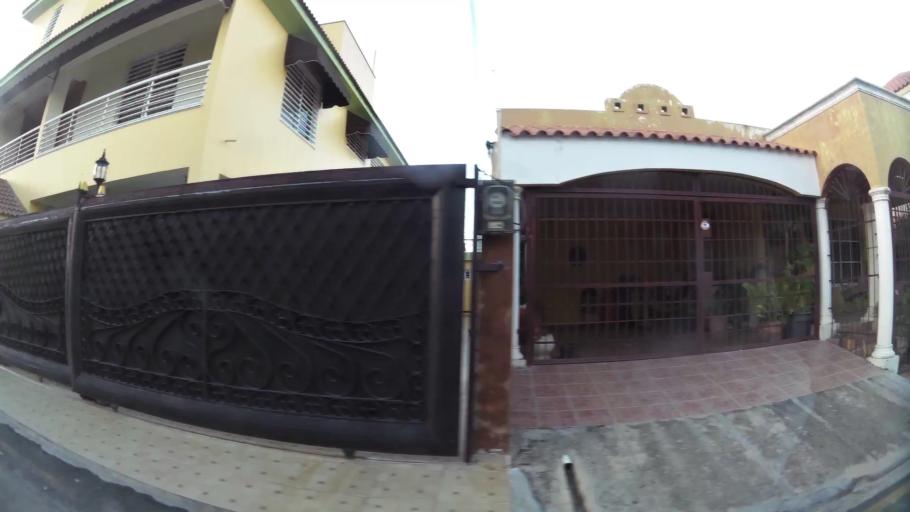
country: DO
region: Santo Domingo
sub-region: Santo Domingo
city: Santo Domingo Este
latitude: 18.4882
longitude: -69.8205
